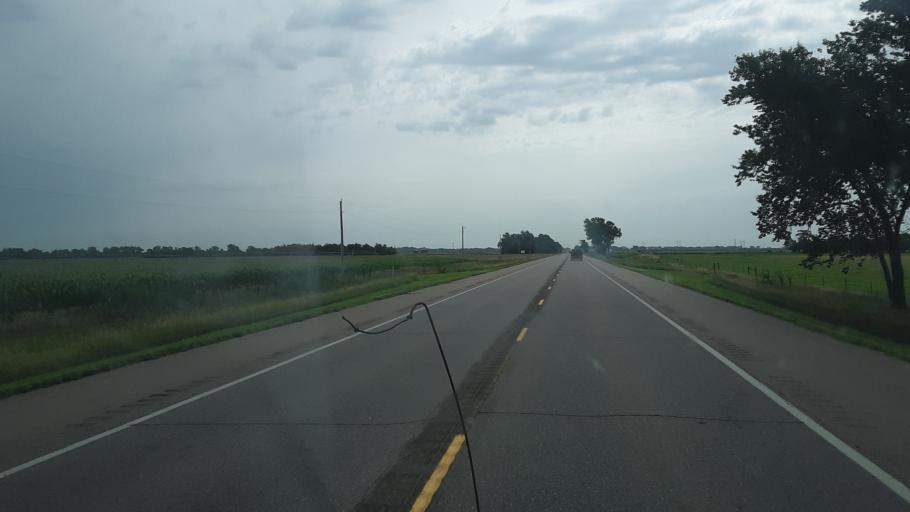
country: US
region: Kansas
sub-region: Stafford County
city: Saint John
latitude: 37.9559
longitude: -98.7616
